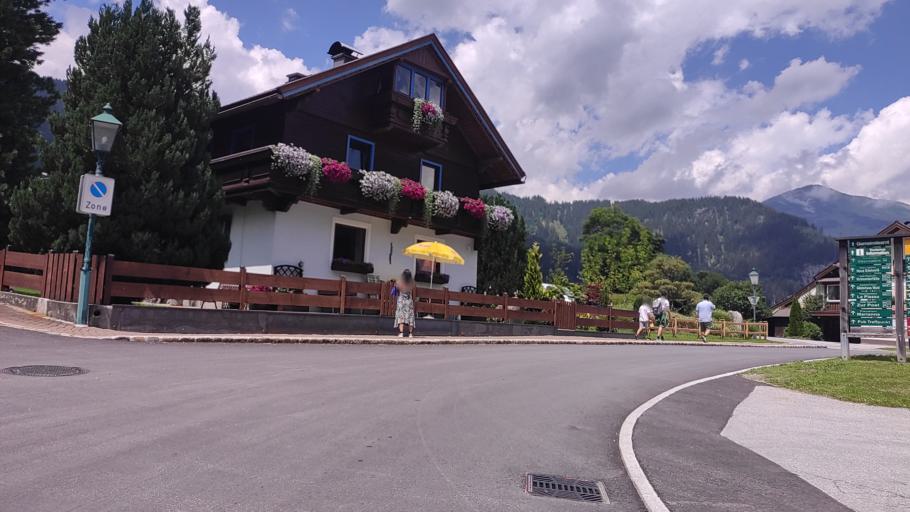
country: AT
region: Salzburg
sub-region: Politischer Bezirk Zell am See
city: Krimml
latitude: 47.2173
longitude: 12.1732
